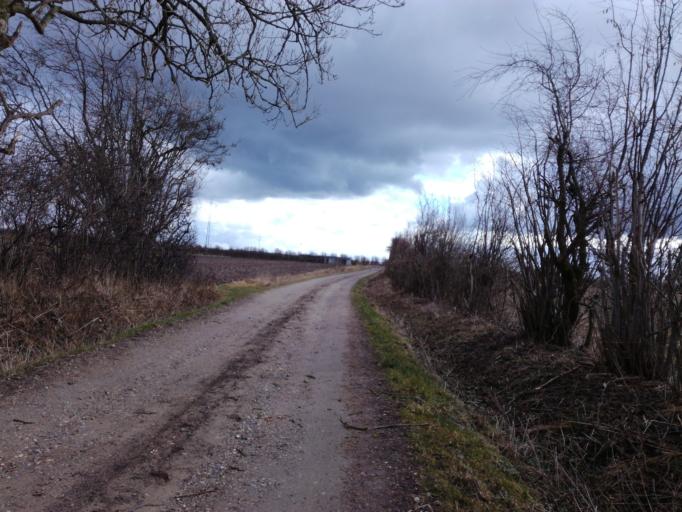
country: DK
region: South Denmark
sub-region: Fredericia Kommune
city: Fredericia
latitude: 55.6091
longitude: 9.7420
